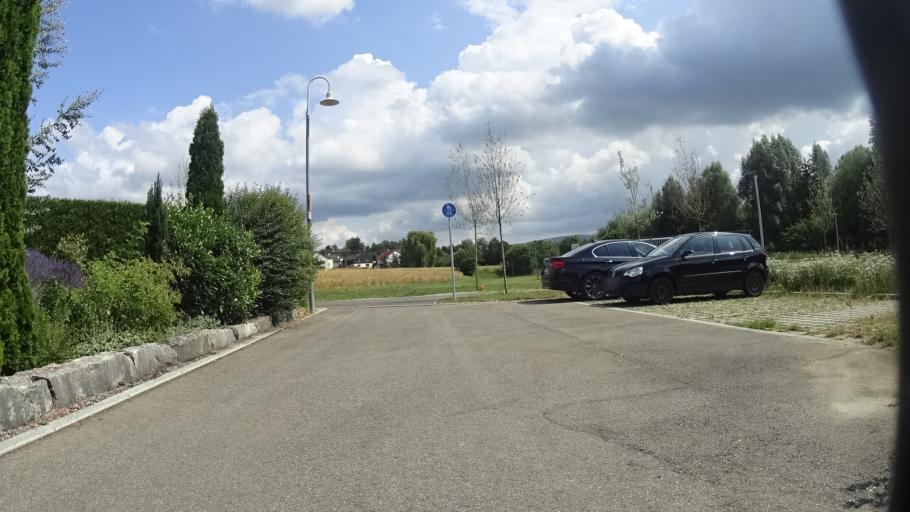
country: DE
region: Baden-Wuerttemberg
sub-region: Regierungsbezirk Stuttgart
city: Eislingen
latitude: 48.6894
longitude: 9.6982
